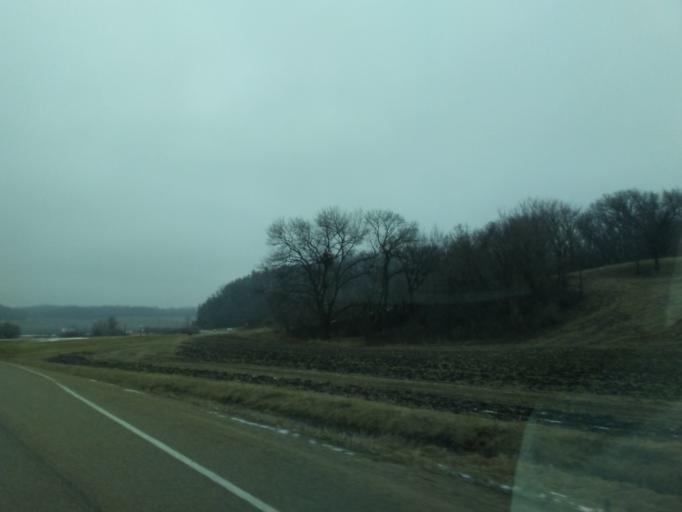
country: US
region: Wisconsin
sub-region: Dane County
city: Black Earth
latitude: 43.1401
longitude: -89.7414
